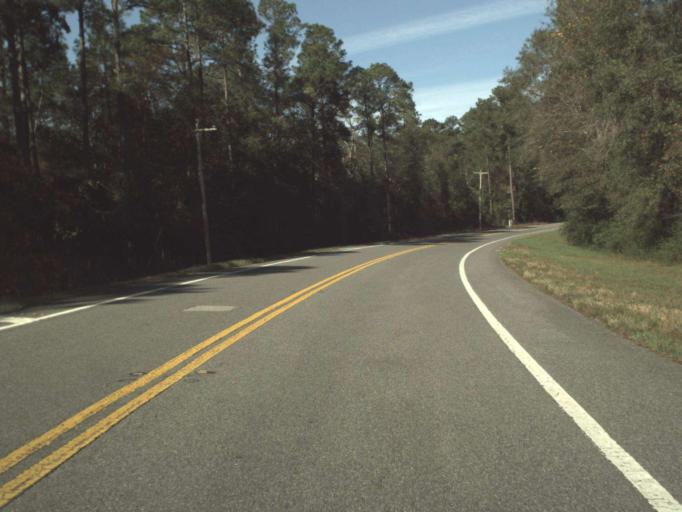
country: US
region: Florida
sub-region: Okaloosa County
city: Crestview
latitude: 30.8356
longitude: -86.7357
